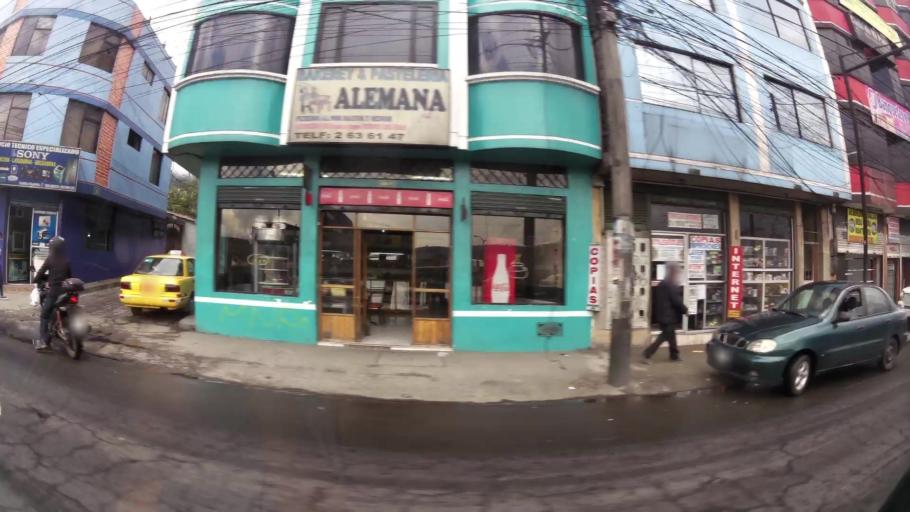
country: EC
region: Pichincha
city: Quito
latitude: -0.2623
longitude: -78.5484
